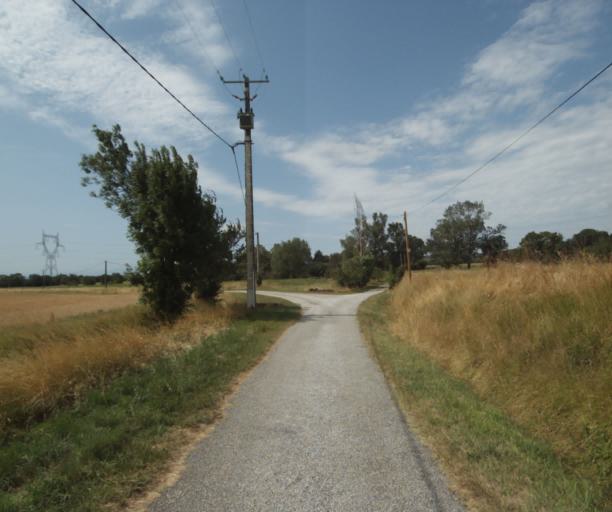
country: FR
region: Midi-Pyrenees
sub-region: Departement de la Haute-Garonne
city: Saint-Felix-Lauragais
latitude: 43.4249
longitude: 1.8946
